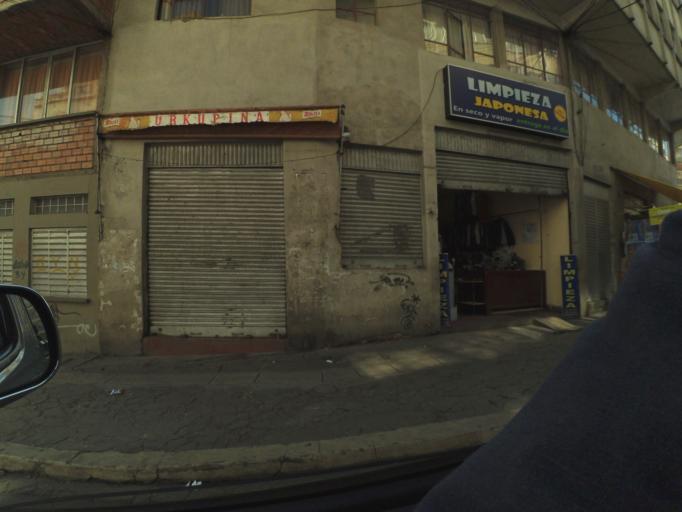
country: BO
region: La Paz
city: La Paz
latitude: -16.4924
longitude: -68.1424
